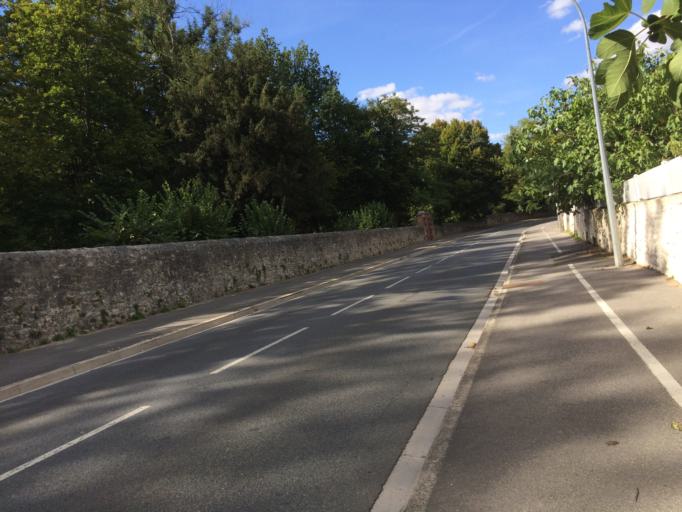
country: FR
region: Ile-de-France
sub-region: Departement de l'Essonne
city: La Ferte-Alais
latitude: 48.4791
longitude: 2.3452
